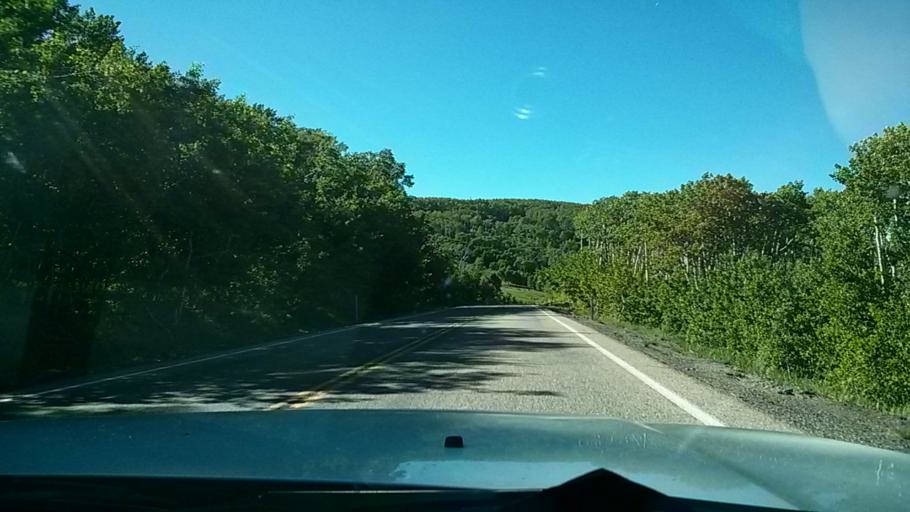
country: US
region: Utah
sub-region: Wayne County
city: Loa
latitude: 38.0451
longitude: -111.3270
